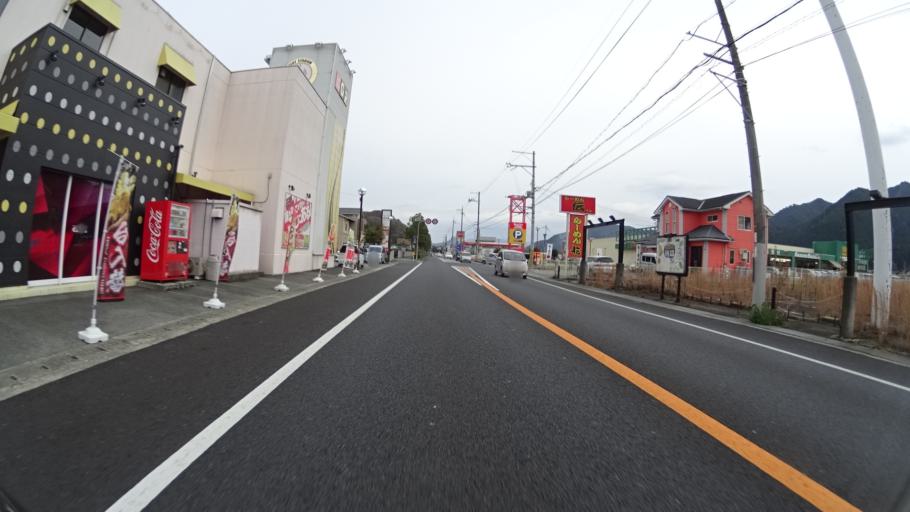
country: JP
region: Hyogo
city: Sasayama
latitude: 35.0644
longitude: 135.1852
